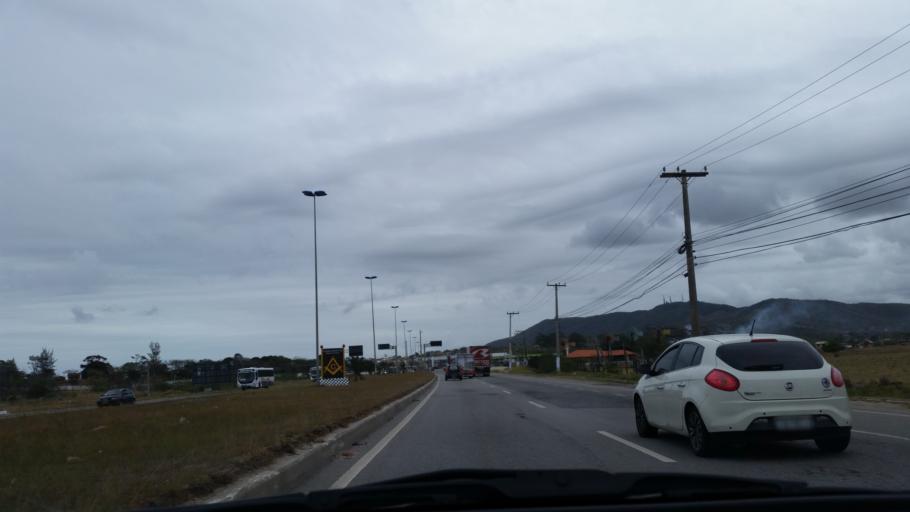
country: BR
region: Rio de Janeiro
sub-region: Sao Pedro Da Aldeia
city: Sao Pedro da Aldeia
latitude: -22.8269
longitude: -42.1192
